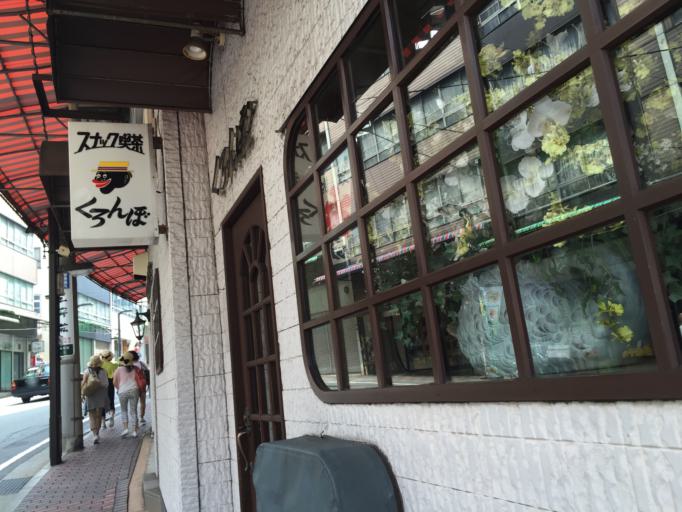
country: JP
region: Shizuoka
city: Atami
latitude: 35.0982
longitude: 139.0738
